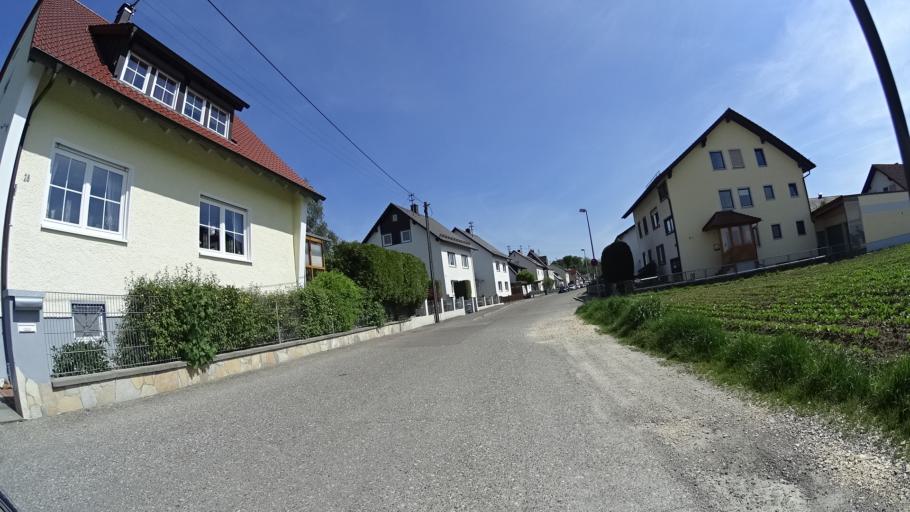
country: DE
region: Bavaria
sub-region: Swabia
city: Weissenhorn
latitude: 48.3111
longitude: 10.1537
